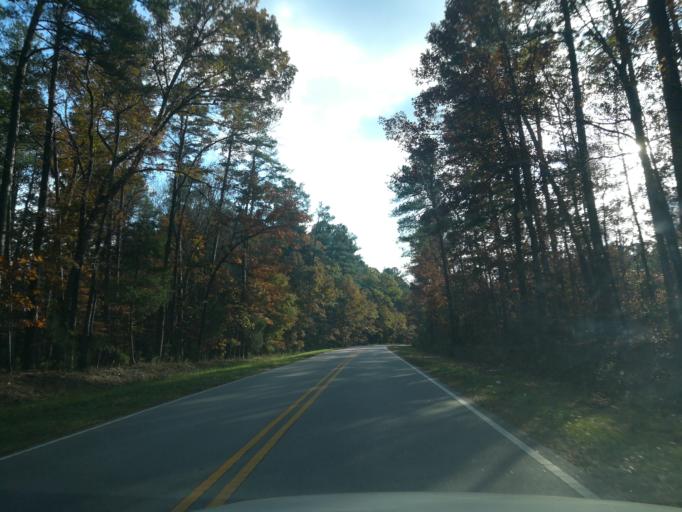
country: US
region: North Carolina
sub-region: Durham County
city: Durham
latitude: 36.0163
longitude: -78.9839
